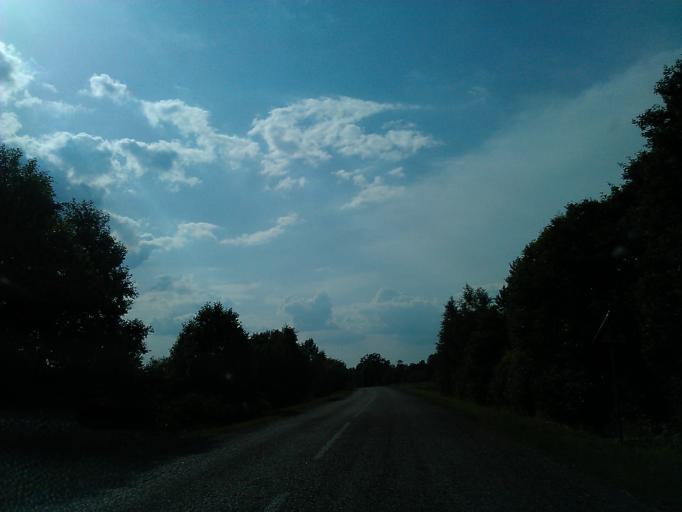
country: LV
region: Skrunda
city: Skrunda
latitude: 56.6970
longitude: 21.8141
